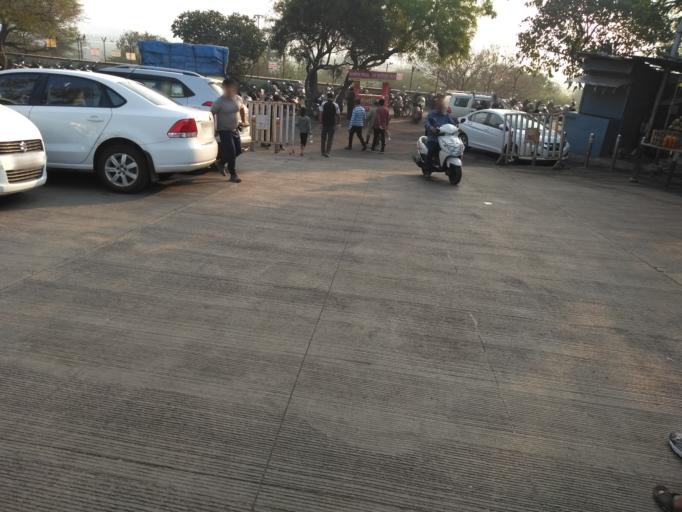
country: IN
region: Maharashtra
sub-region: Pune Division
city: Pune
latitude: 18.4759
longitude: 73.8445
